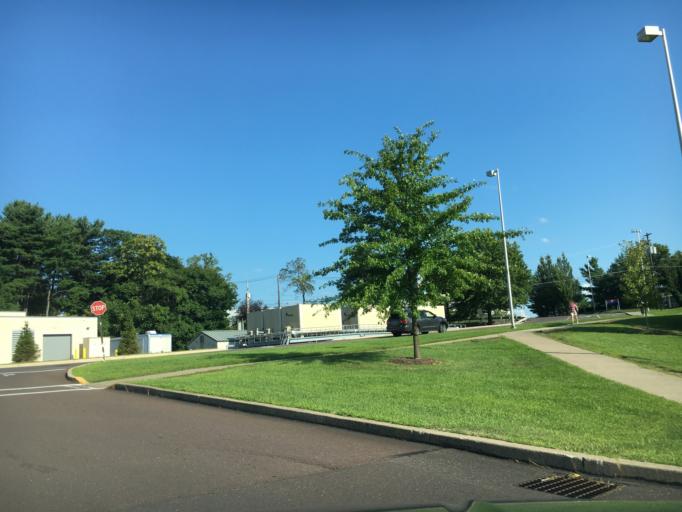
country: US
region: Pennsylvania
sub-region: Montour County
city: Danville
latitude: 40.9704
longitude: -76.6068
